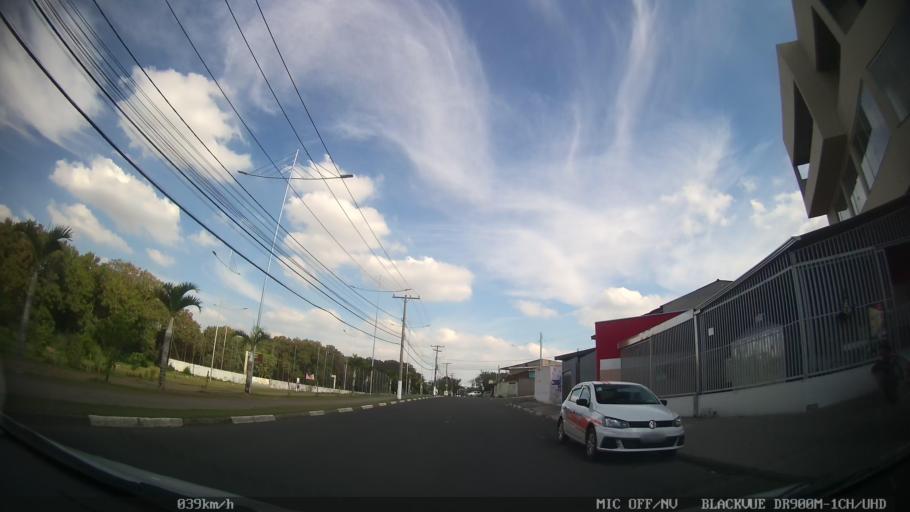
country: BR
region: Sao Paulo
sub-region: Hortolandia
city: Hortolandia
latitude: -22.8942
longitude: -47.2398
